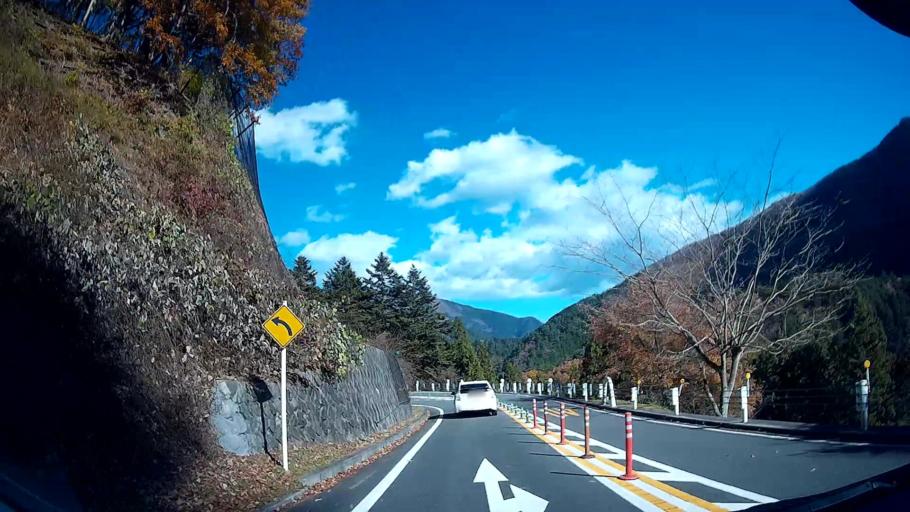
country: JP
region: Yamanashi
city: Uenohara
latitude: 35.7673
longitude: 139.0204
